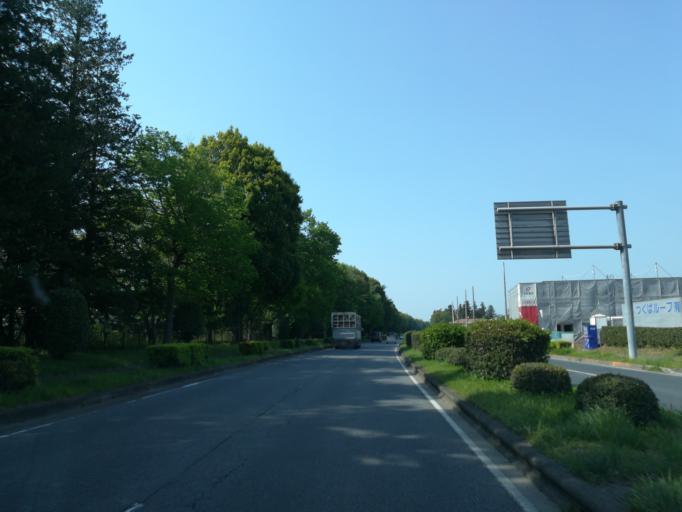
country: JP
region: Ibaraki
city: Tsukuba
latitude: 36.1124
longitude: 140.0743
